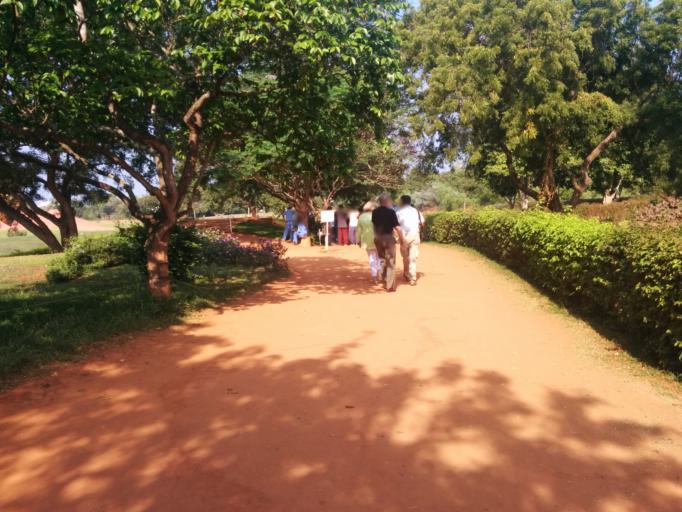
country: IN
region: Tamil Nadu
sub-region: Villupuram
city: Auroville
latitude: 12.0050
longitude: 79.8100
